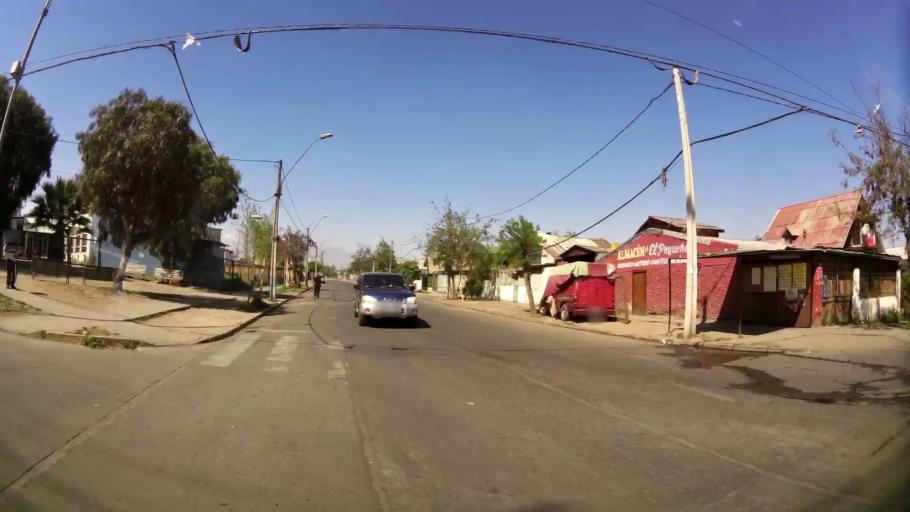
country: CL
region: Santiago Metropolitan
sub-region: Provincia de Santiago
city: Lo Prado
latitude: -33.5018
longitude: -70.7339
